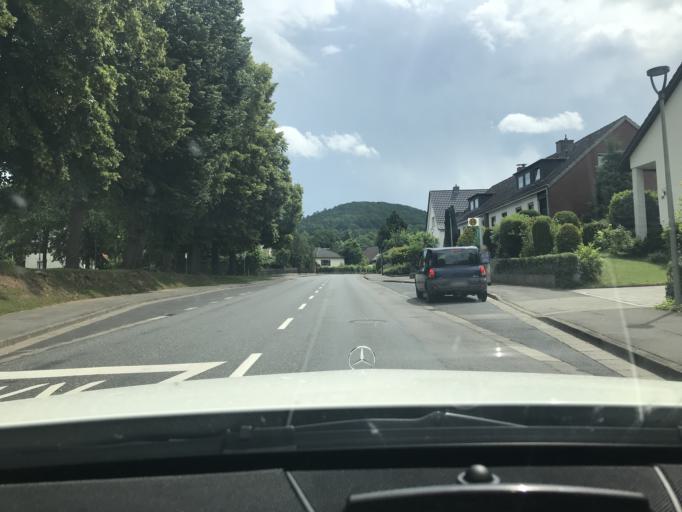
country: DE
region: Hesse
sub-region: Regierungsbezirk Kassel
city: Eschwege
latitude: 51.1830
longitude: 10.0684
